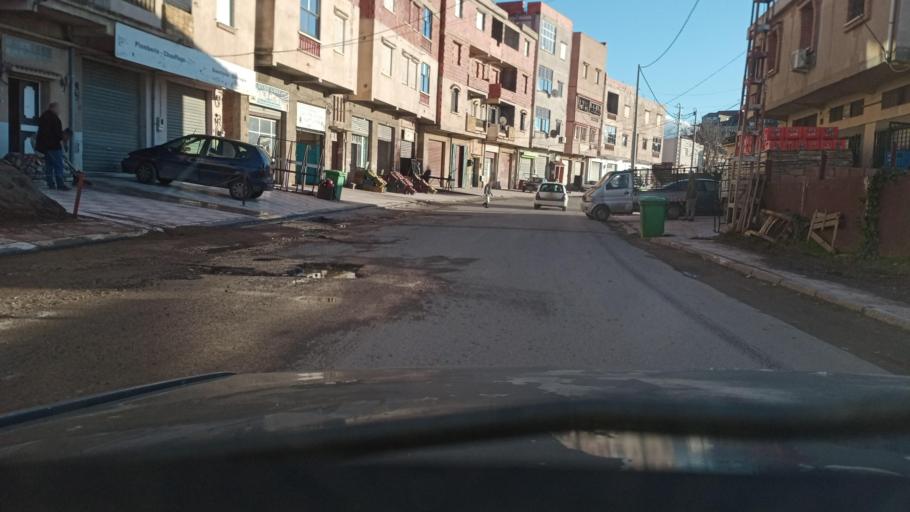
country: DZ
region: Tizi Ouzou
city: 'Ain el Hammam
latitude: 36.5622
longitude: 4.3241
